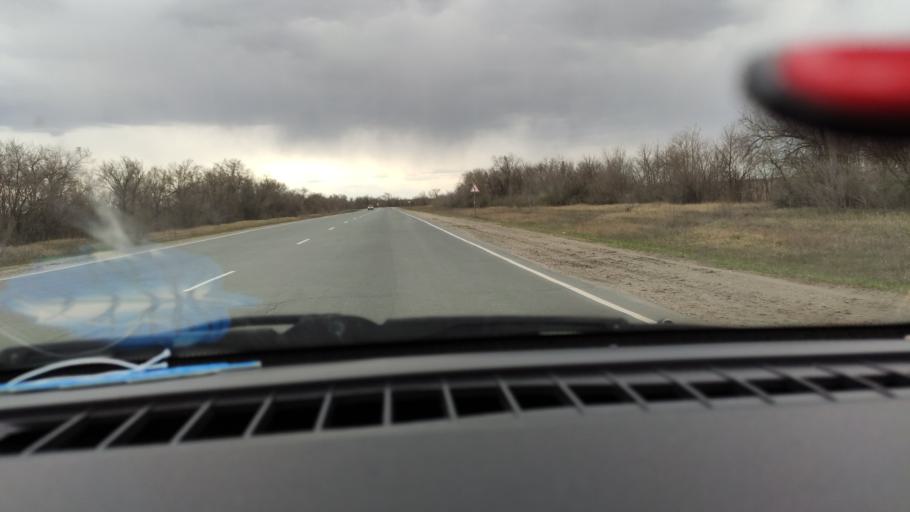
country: RU
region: Saratov
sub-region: Saratovskiy Rayon
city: Saratov
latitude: 51.7080
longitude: 46.0155
